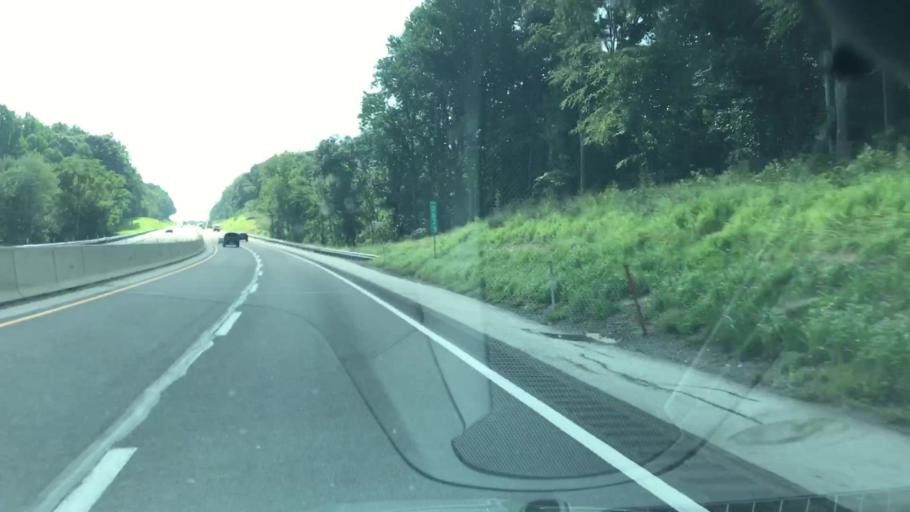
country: US
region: Pennsylvania
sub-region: Lebanon County
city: Cornwall
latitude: 40.2280
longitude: -76.4917
